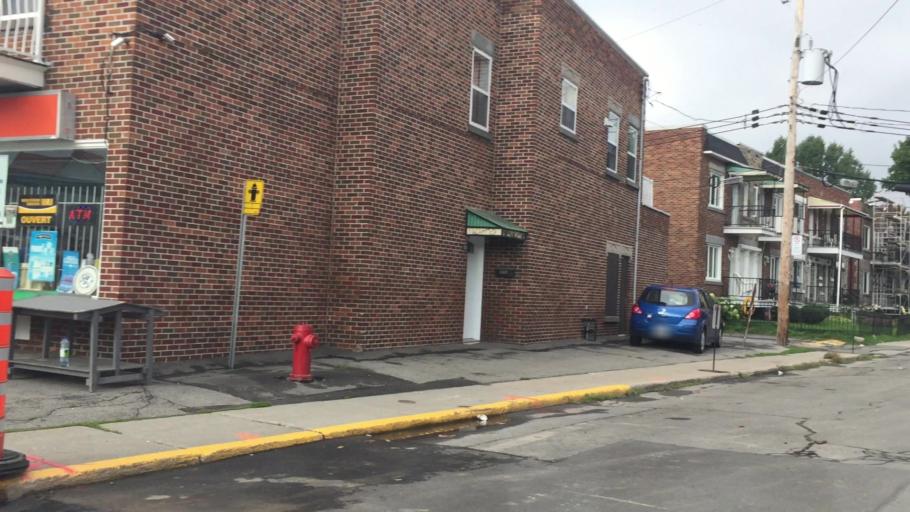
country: CA
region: Quebec
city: Saint-Raymond
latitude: 45.4449
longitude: -73.5775
